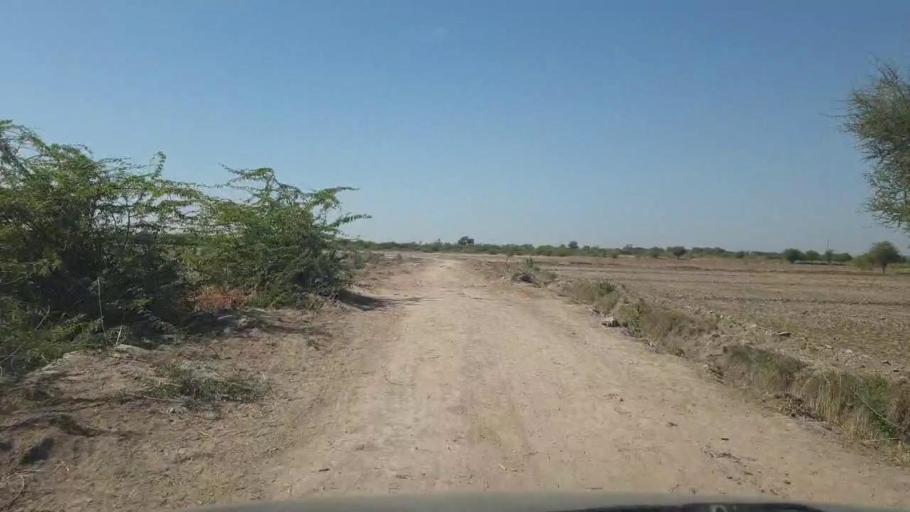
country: PK
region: Sindh
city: Dhoro Naro
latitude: 25.4457
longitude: 69.6124
